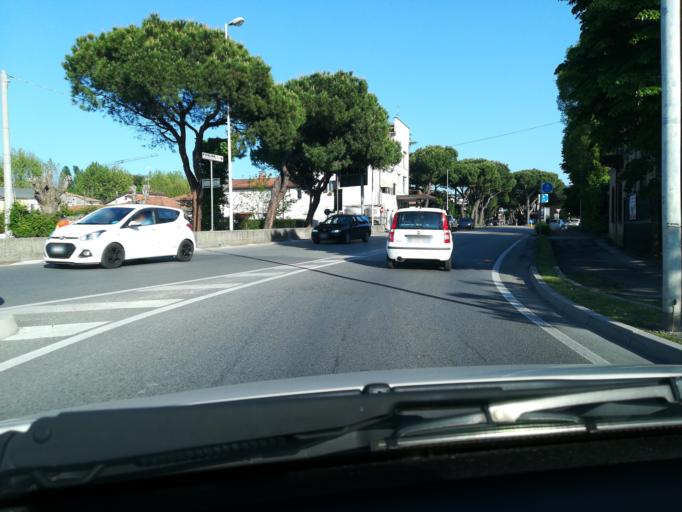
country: IT
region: Emilia-Romagna
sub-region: Provincia di Rimini
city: Riccione
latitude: 43.9983
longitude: 12.6472
